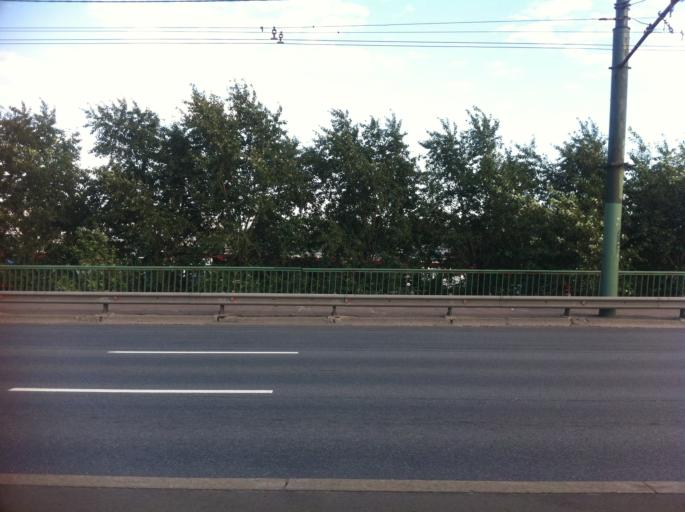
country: RU
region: St.-Petersburg
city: Avtovo
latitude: 59.8665
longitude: 30.2430
